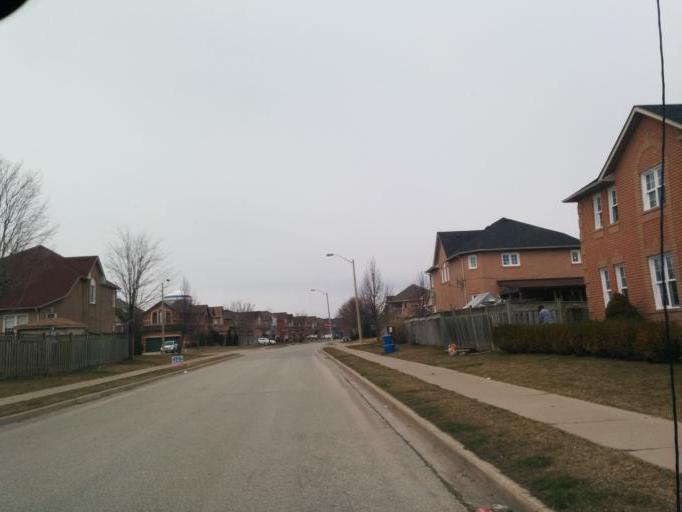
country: CA
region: Ontario
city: Brampton
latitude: 43.7277
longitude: -79.8225
